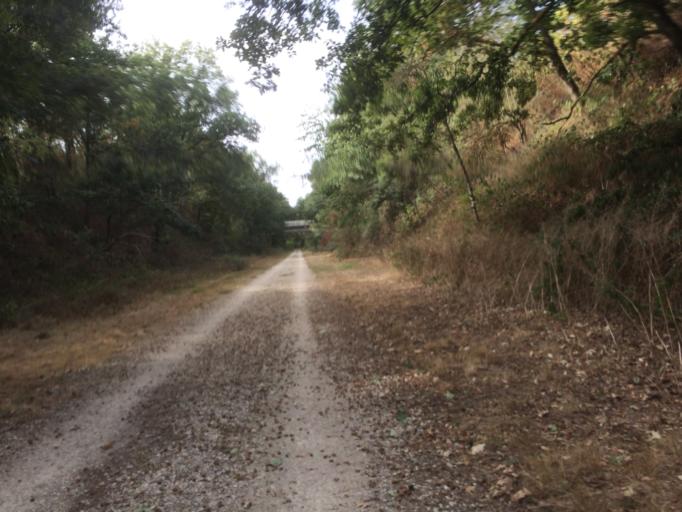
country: FR
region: Ile-de-France
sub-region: Departement des Yvelines
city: Bonnelles
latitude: 48.6319
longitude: 2.0434
